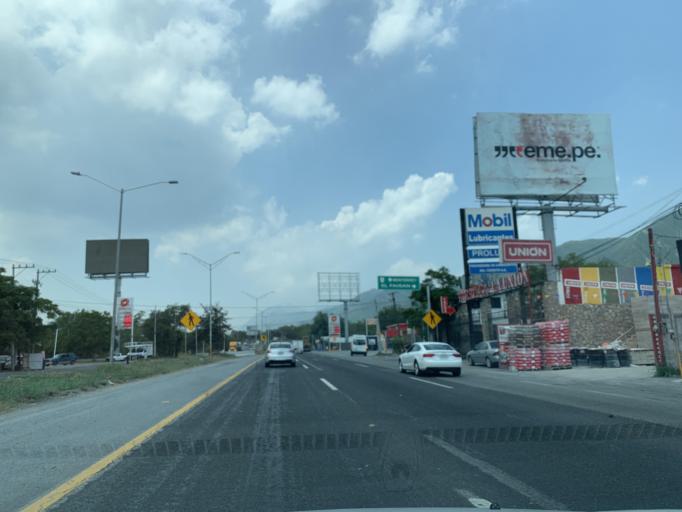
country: MX
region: Nuevo Leon
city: Santiago
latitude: 25.5079
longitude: -100.1941
